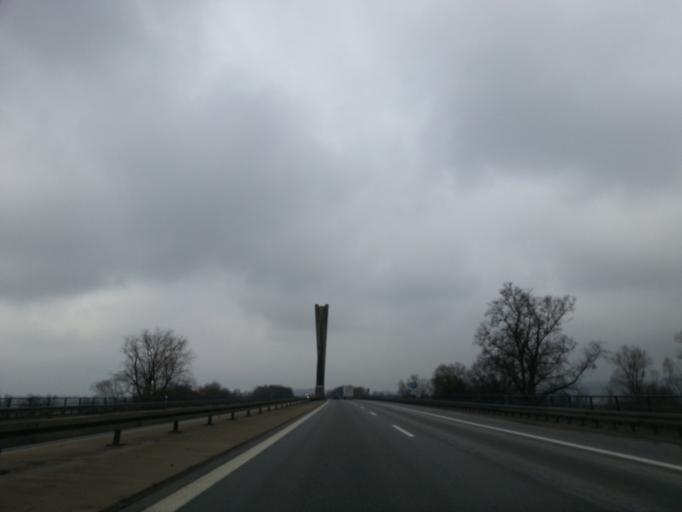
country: DE
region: Bavaria
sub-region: Lower Bavaria
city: Metten
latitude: 48.8423
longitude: 12.8958
